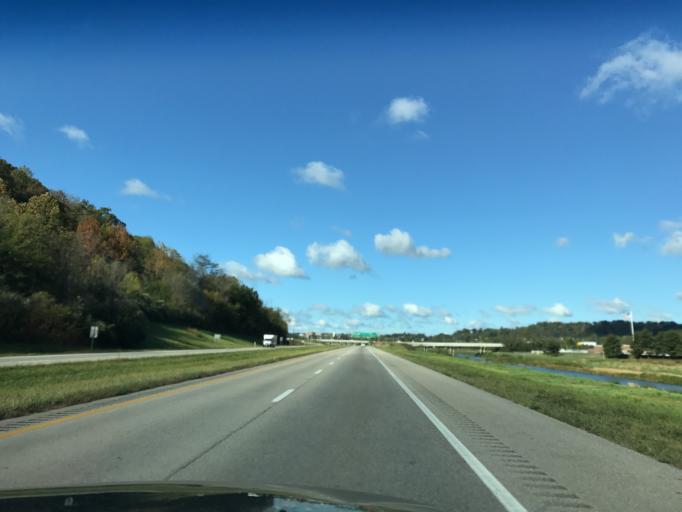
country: US
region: Ohio
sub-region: Athens County
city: Athens
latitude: 39.3324
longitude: -82.0734
